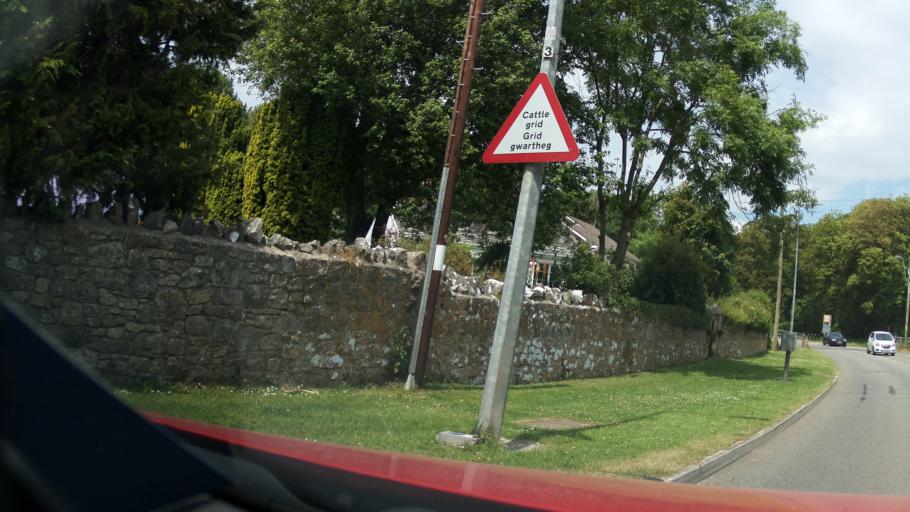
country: GB
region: Wales
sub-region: Bridgend county borough
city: Merthyr Mawr
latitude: 51.4647
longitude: -3.5894
